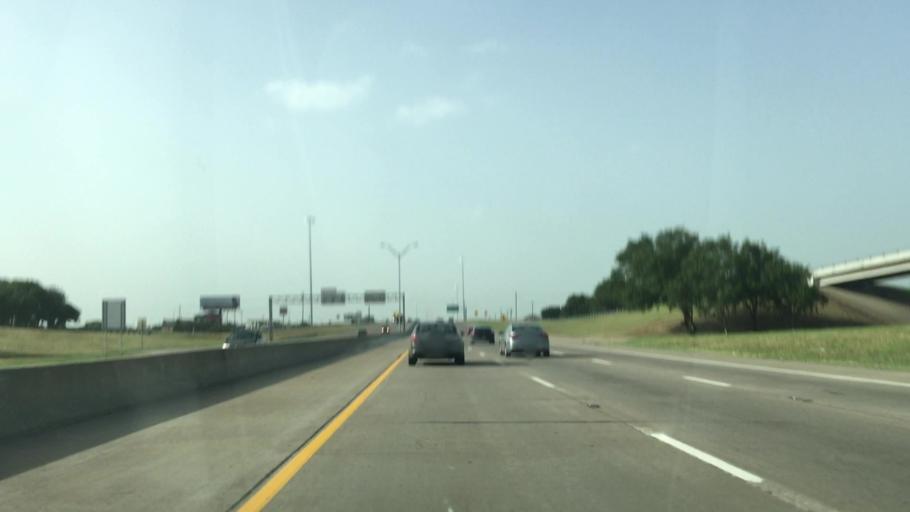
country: US
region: Texas
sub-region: Dallas County
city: DeSoto
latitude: 32.6441
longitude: -96.8232
